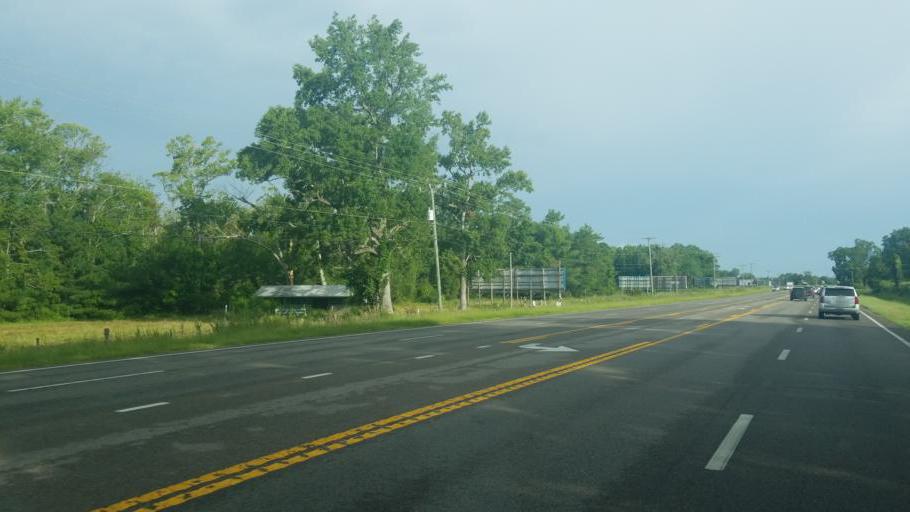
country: US
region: North Carolina
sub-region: Currituck County
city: Currituck
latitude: 36.3212
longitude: -75.9398
